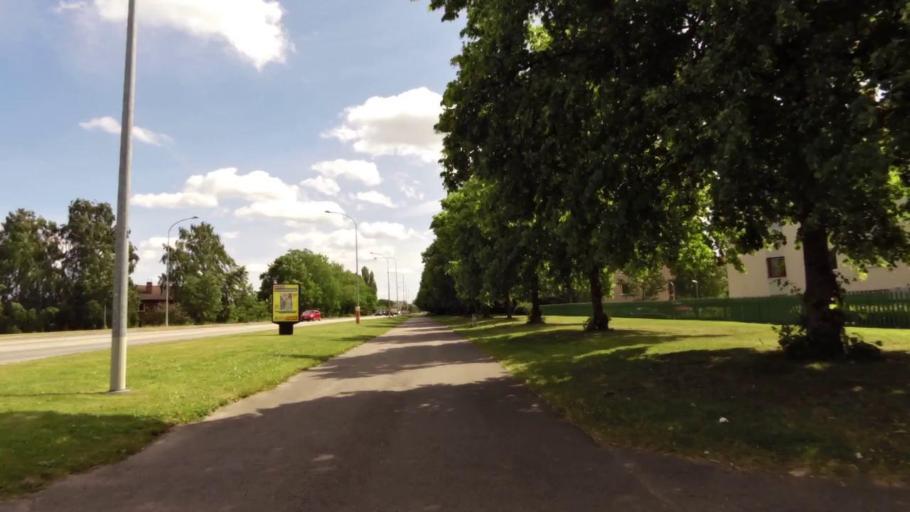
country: SE
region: OEstergoetland
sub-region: Linkopings Kommun
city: Linkoping
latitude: 58.4188
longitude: 15.5981
